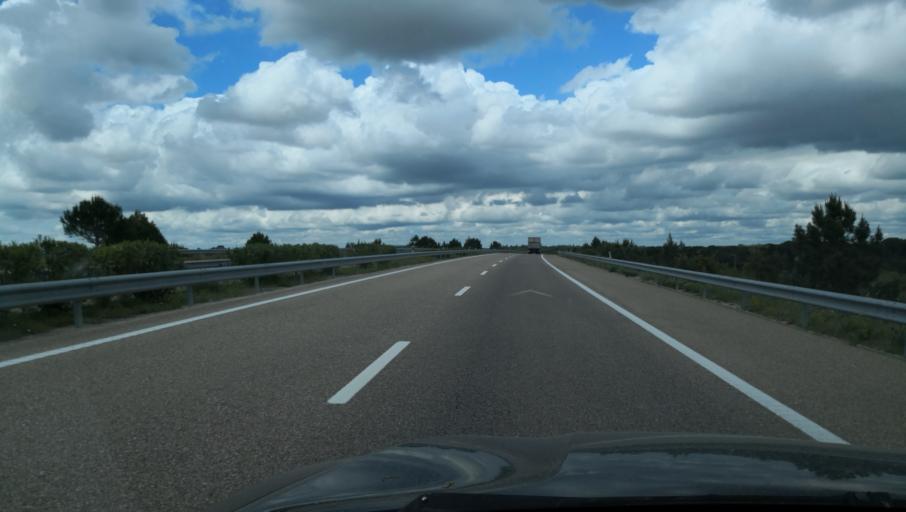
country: PT
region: Evora
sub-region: Vendas Novas
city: Vendas Novas
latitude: 38.6453
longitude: -8.6659
